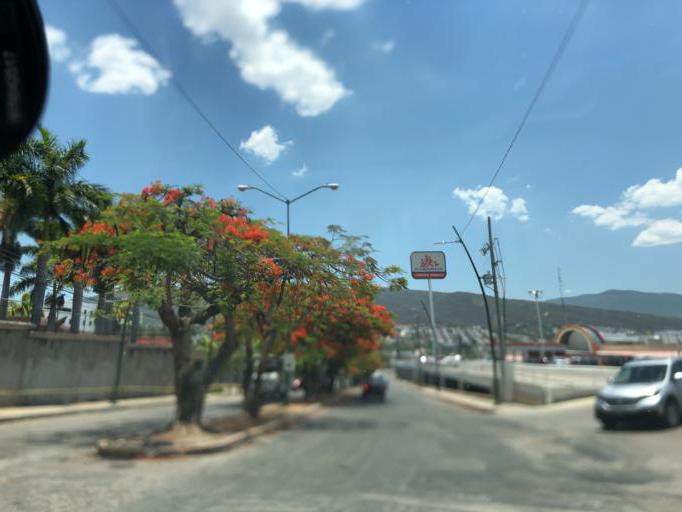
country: MX
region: Chiapas
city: Tuxtla Gutierrez
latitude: 16.7522
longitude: -93.1509
